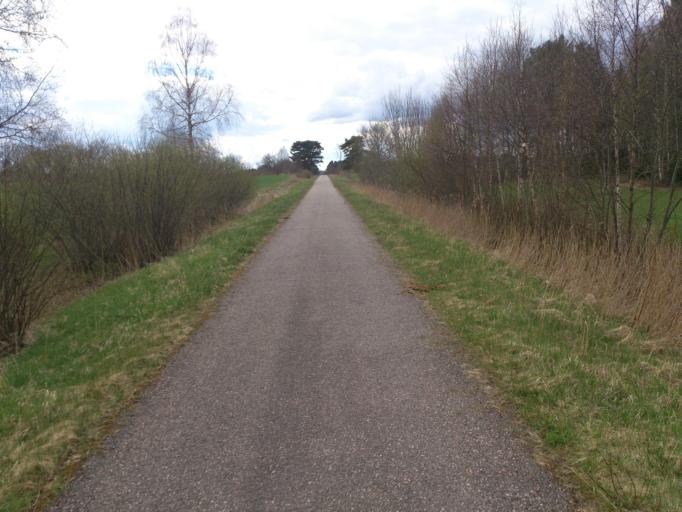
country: SE
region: Vaestra Goetaland
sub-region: Ulricehamns Kommun
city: Ulricehamn
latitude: 57.9698
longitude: 13.5177
